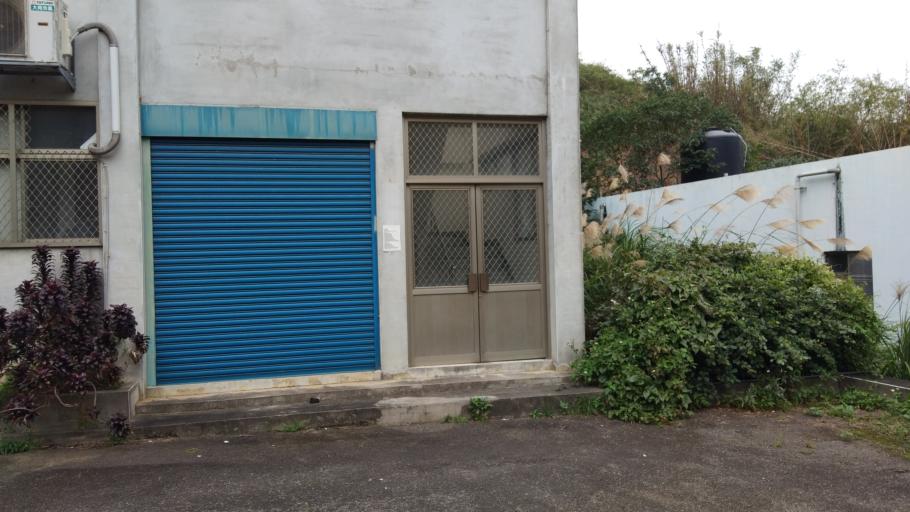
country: TW
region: Taiwan
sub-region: Hsinchu
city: Hsinchu
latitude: 24.7628
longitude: 120.9551
